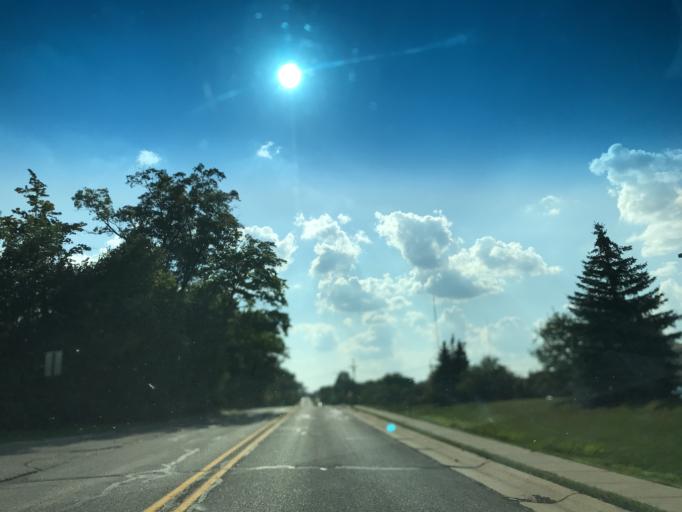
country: US
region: Michigan
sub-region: Oakland County
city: Novi
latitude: 42.4818
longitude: -83.4535
